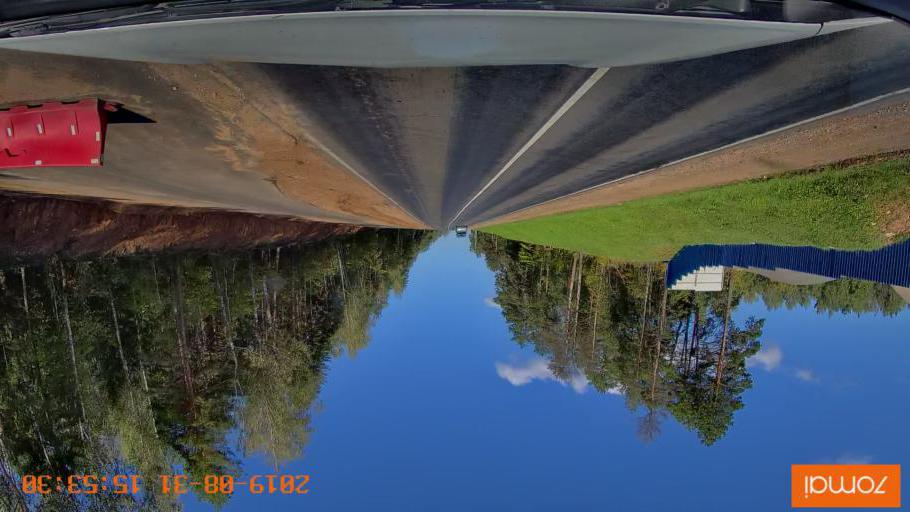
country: RU
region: Kaluga
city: Yukhnov
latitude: 54.7131
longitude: 35.1322
